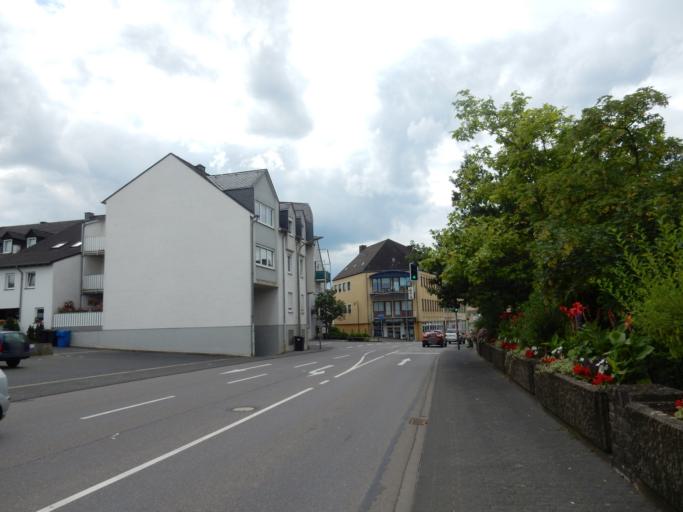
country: DE
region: Rheinland-Pfalz
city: Bitburg
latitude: 49.9756
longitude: 6.5269
